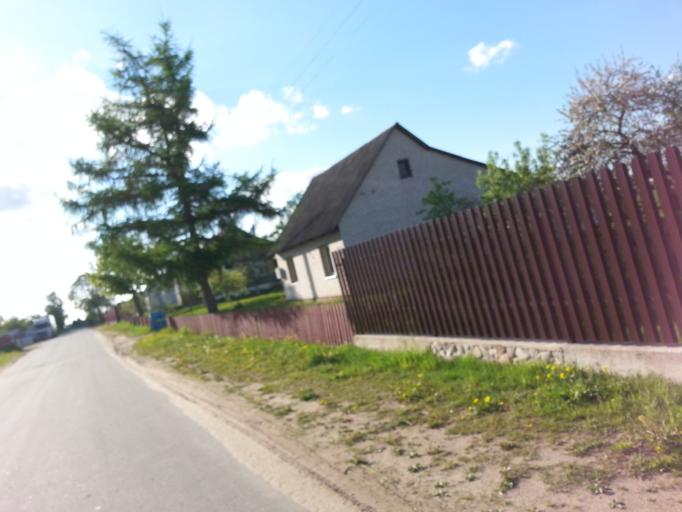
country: BY
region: Minsk
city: Narach
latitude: 54.9341
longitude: 26.7028
